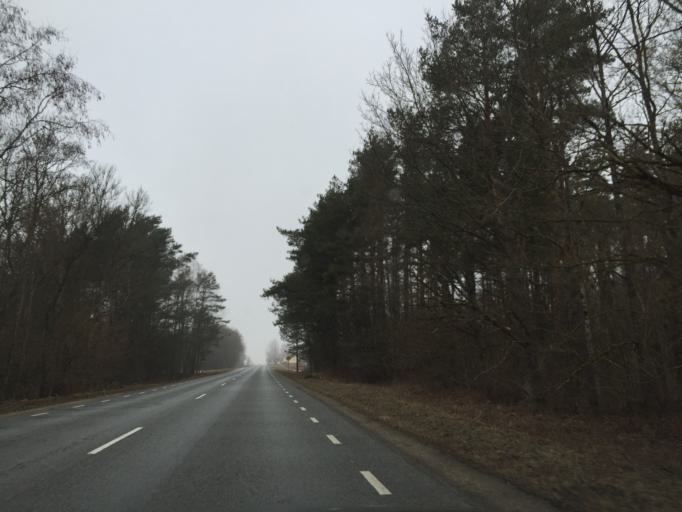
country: EE
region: Laeaene
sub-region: Lihula vald
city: Lihula
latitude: 58.5702
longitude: 23.7488
